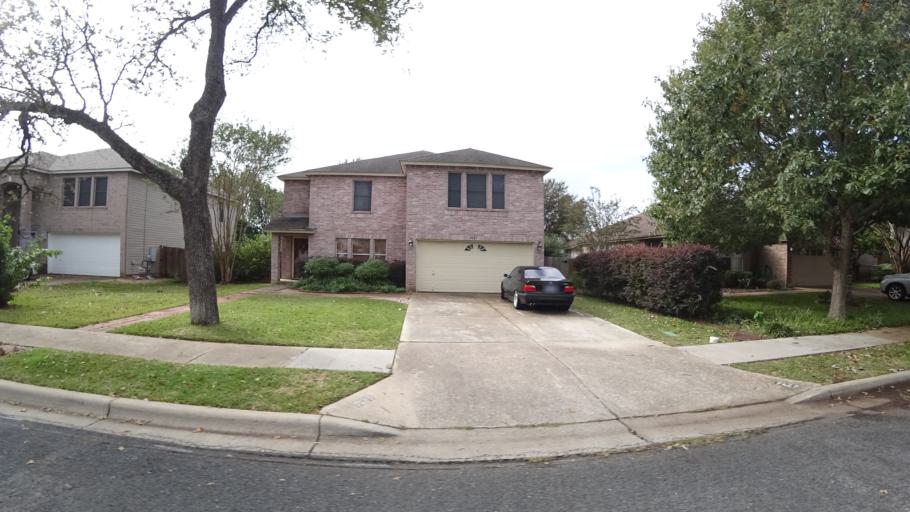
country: US
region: Texas
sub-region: Travis County
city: Shady Hollow
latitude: 30.2137
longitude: -97.8441
